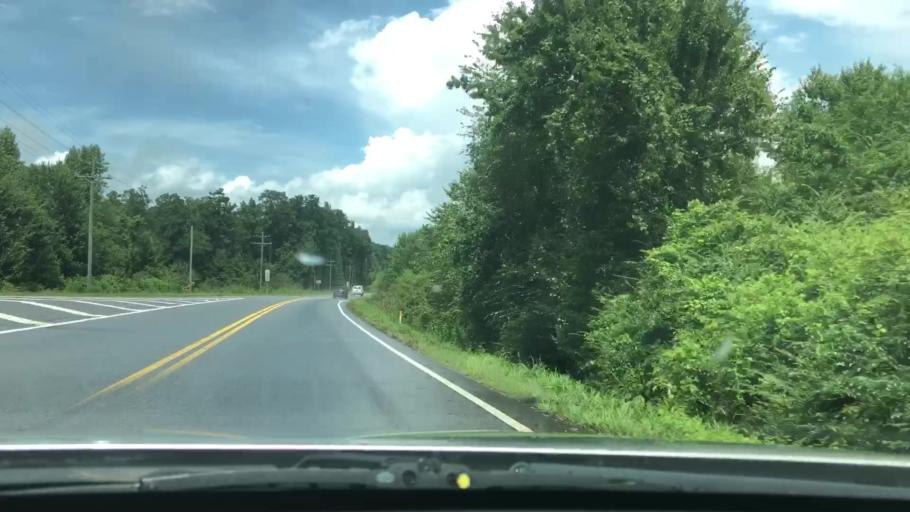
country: US
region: Georgia
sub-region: Lamar County
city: Barnesville
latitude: 33.0859
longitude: -84.1545
